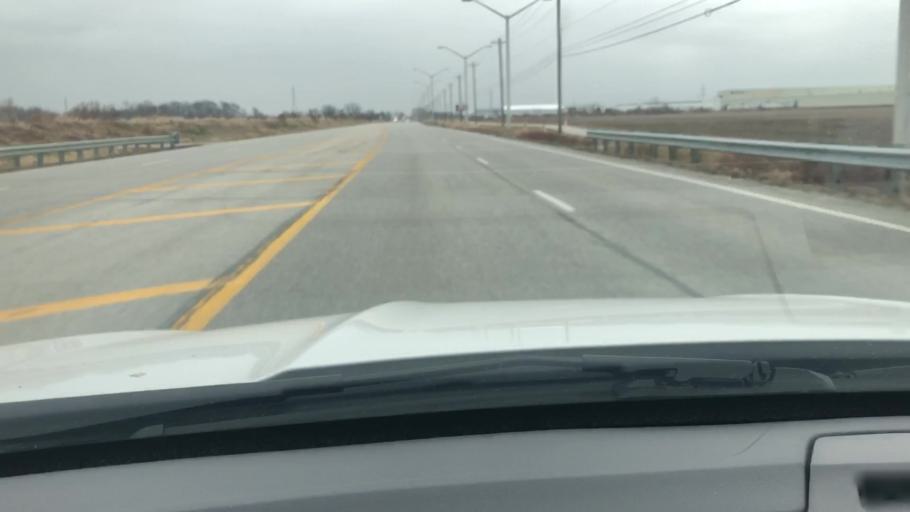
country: US
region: Indiana
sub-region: Tippecanoe County
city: Lafayette
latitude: 40.3673
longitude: -86.8439
